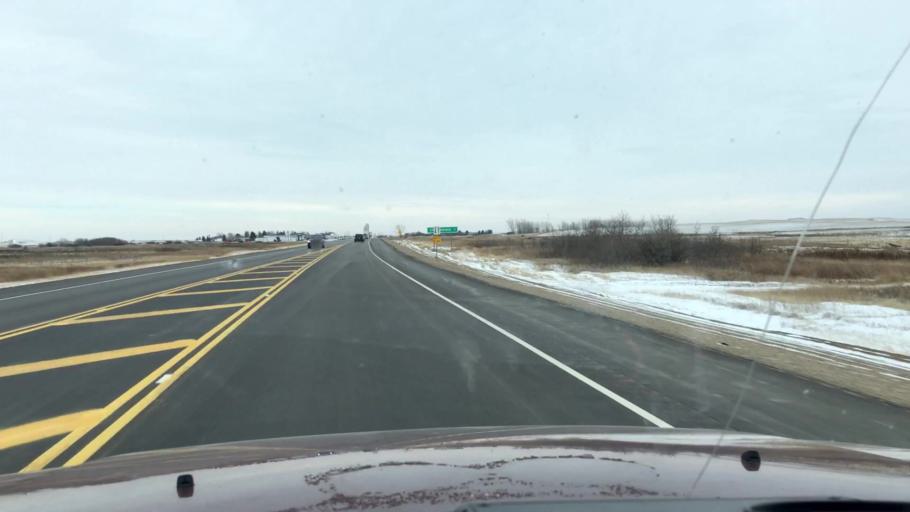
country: CA
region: Saskatchewan
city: Moose Jaw
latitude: 50.8604
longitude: -105.5866
